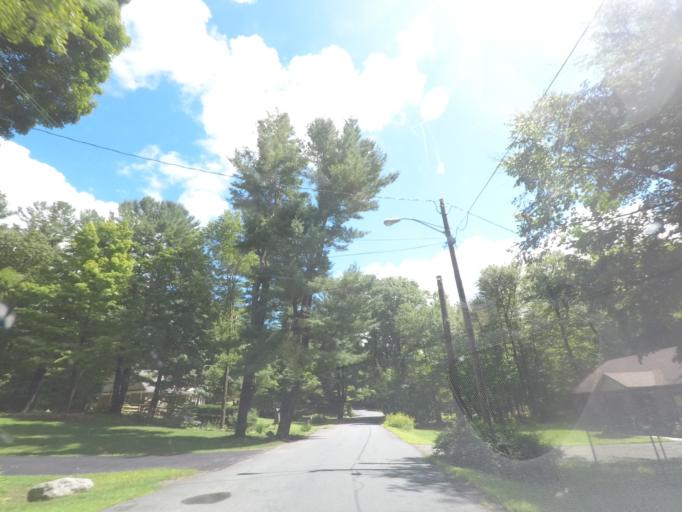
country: US
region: New York
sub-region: Rensselaer County
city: West Sand Lake
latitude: 42.6429
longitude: -73.5842
